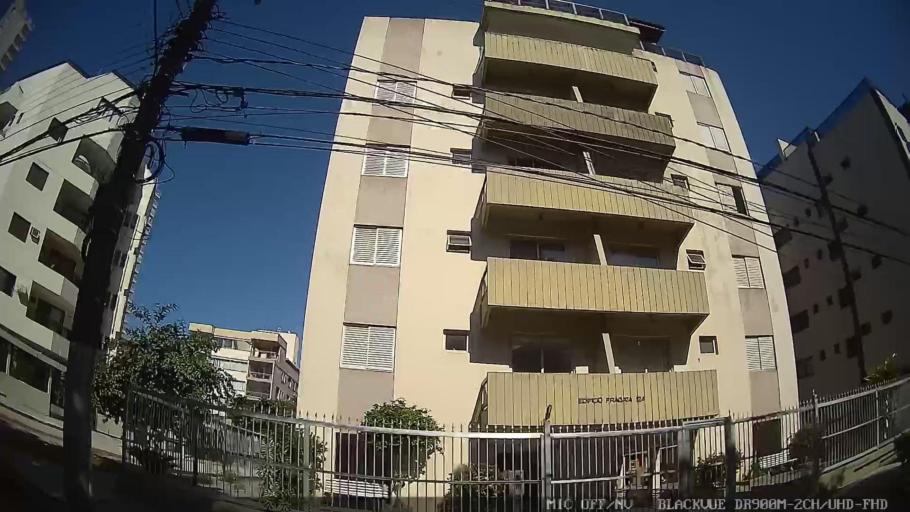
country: BR
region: Sao Paulo
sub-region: Guaruja
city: Guaruja
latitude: -23.9815
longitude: -46.2074
